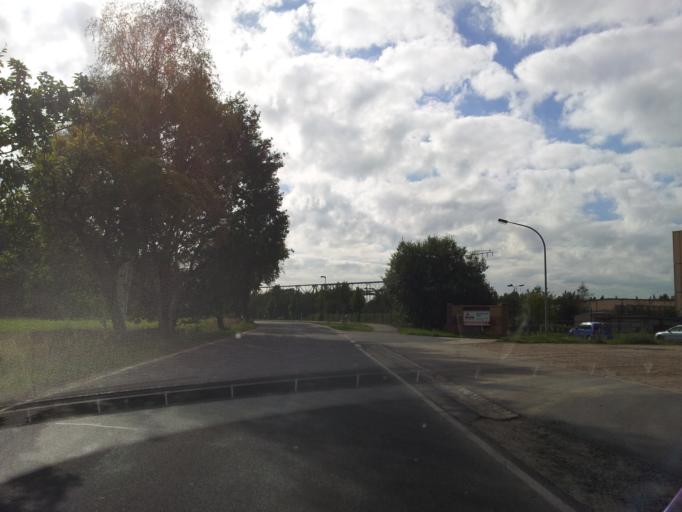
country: DE
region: Brandenburg
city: Sallgast
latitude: 51.5930
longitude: 13.7774
